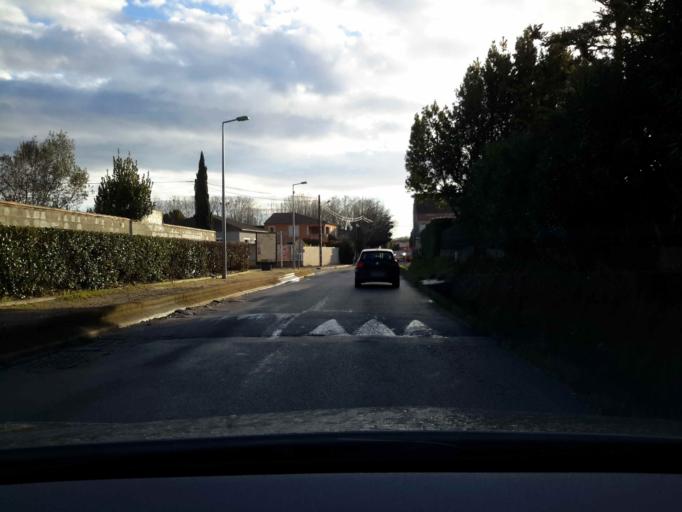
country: FR
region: Languedoc-Roussillon
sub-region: Departement du Gard
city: Generac
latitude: 43.7290
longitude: 4.3420
